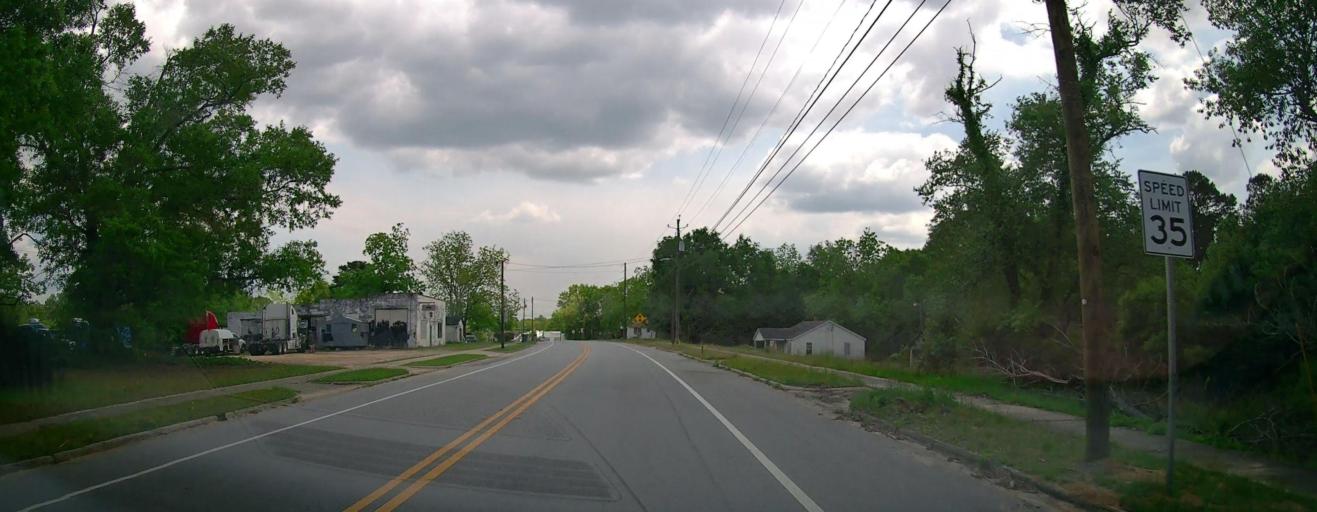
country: US
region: Georgia
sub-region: Treutlen County
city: Soperton
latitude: 32.3823
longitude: -82.5954
